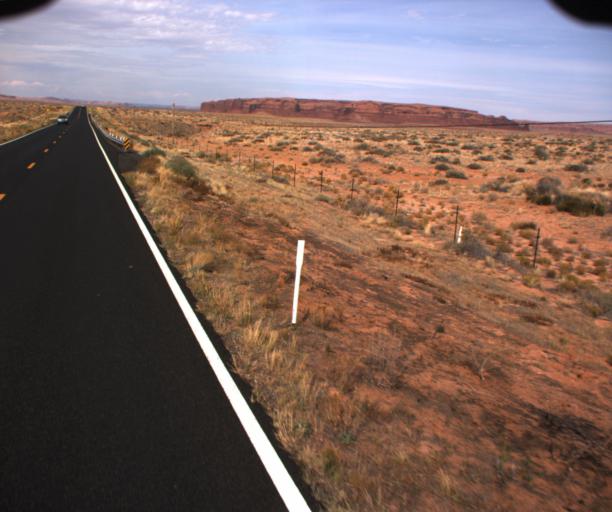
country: US
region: Arizona
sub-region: Apache County
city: Many Farms
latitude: 36.5643
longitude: -109.5428
